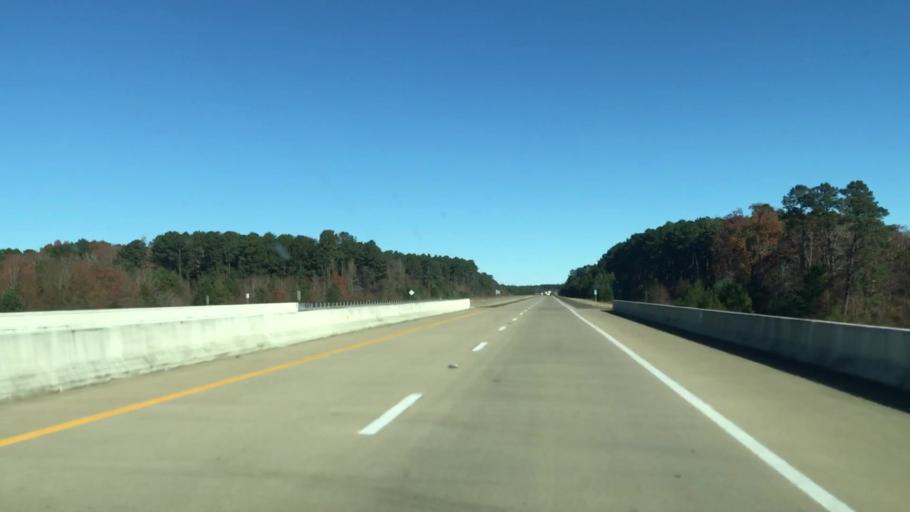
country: US
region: Louisiana
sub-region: Caddo Parish
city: Vivian
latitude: 33.0919
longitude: -93.8947
